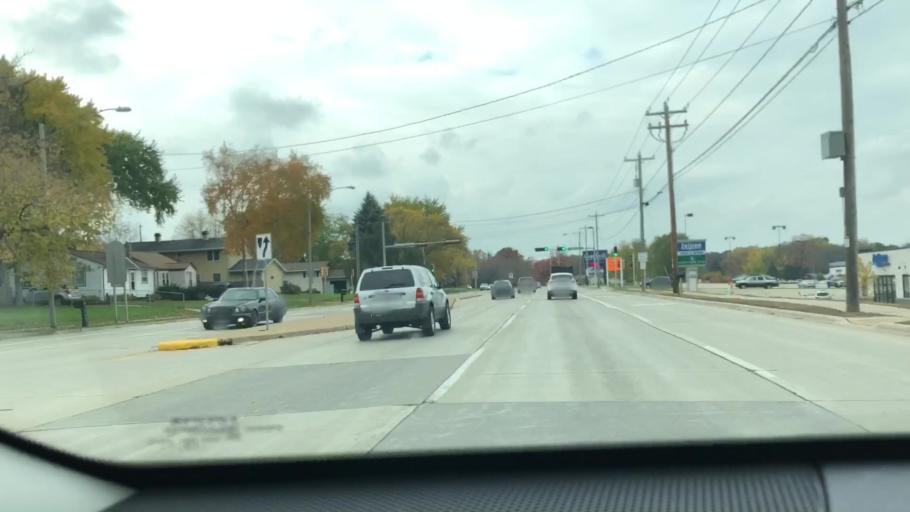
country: US
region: Wisconsin
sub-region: Brown County
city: Howard
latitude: 44.5241
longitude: -88.0651
